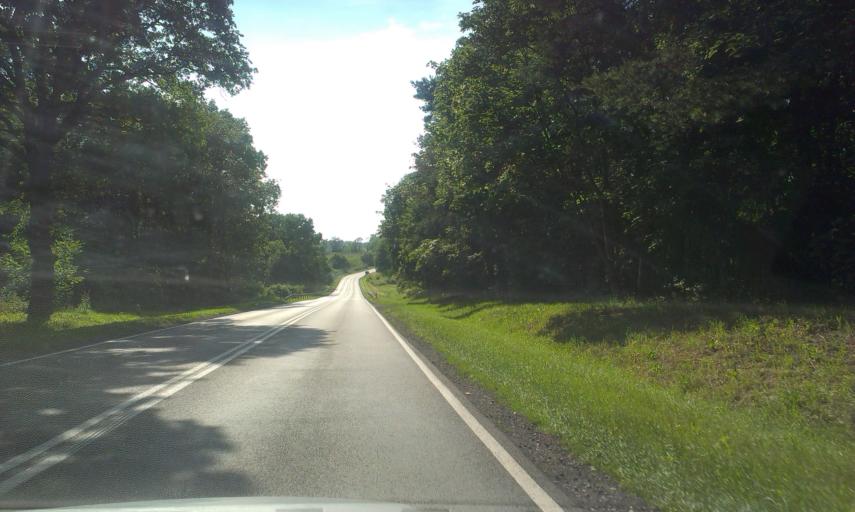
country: PL
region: Kujawsko-Pomorskie
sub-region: Powiat bydgoski
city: Biale Blota
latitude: 53.1562
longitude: 17.8710
